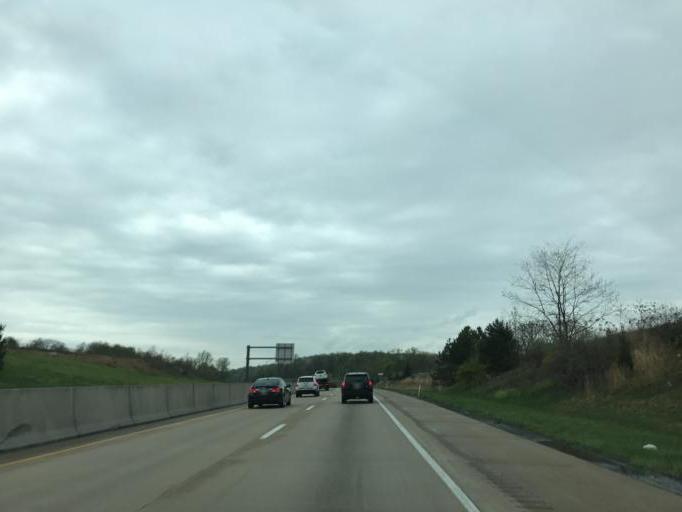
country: US
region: Pennsylvania
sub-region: Berks County
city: Mohnton
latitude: 40.2741
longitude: -76.0229
